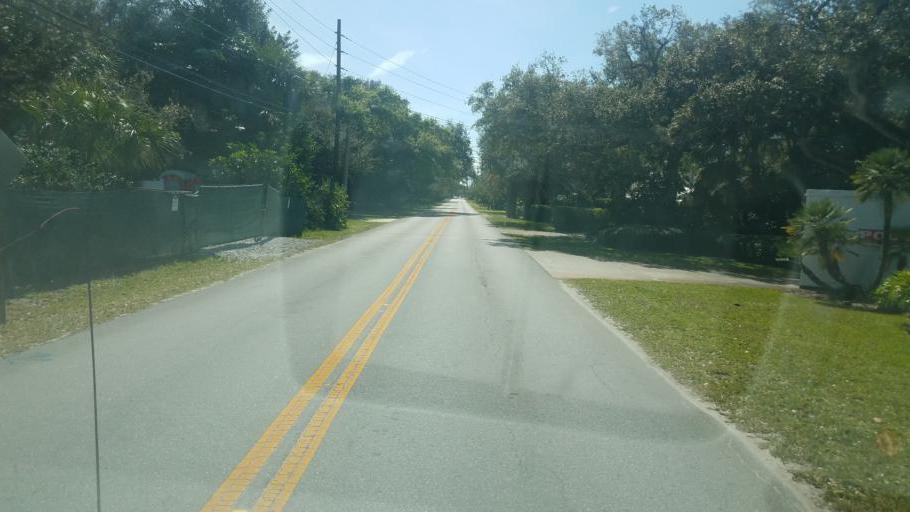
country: US
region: Florida
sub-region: Indian River County
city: Vero Beach
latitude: 27.6403
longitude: -80.3565
